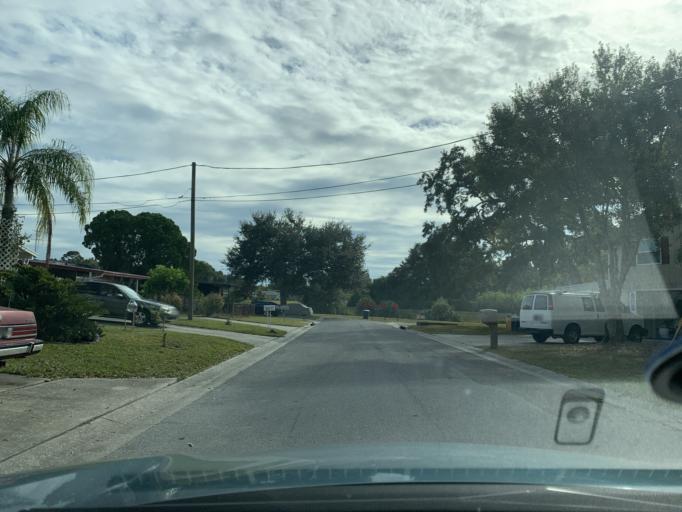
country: US
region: Florida
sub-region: Pinellas County
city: Kenneth City
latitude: 27.8120
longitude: -82.7358
